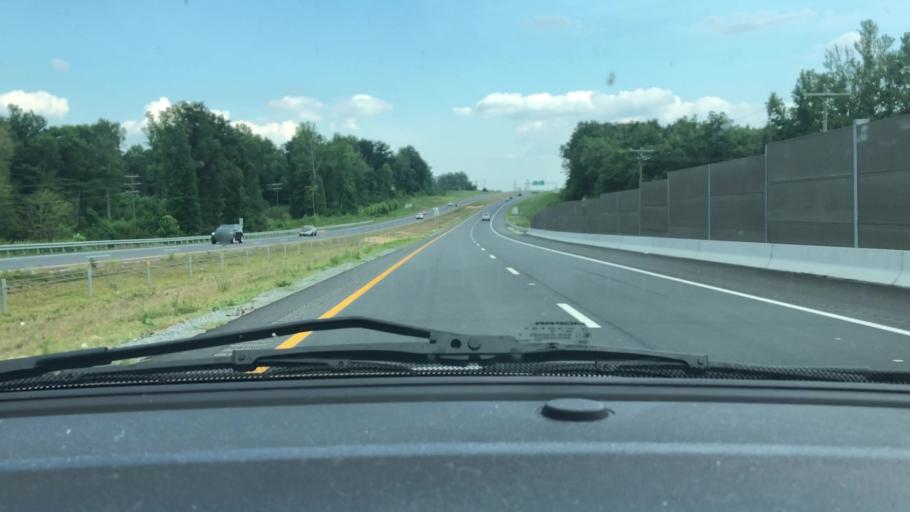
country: US
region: North Carolina
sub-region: Guilford County
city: Summerfield
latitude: 36.2573
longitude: -79.9249
